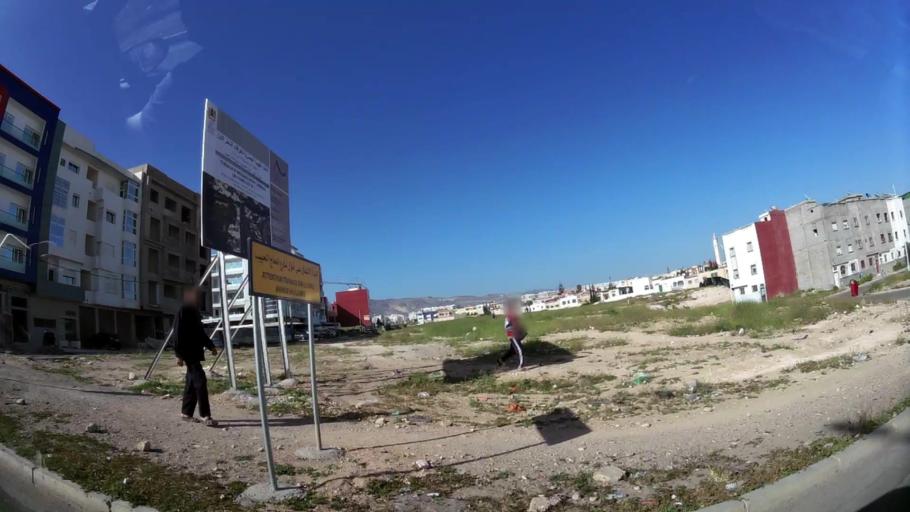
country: MA
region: Souss-Massa-Draa
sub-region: Agadir-Ida-ou-Tnan
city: Agadir
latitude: 30.4260
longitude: -9.5760
